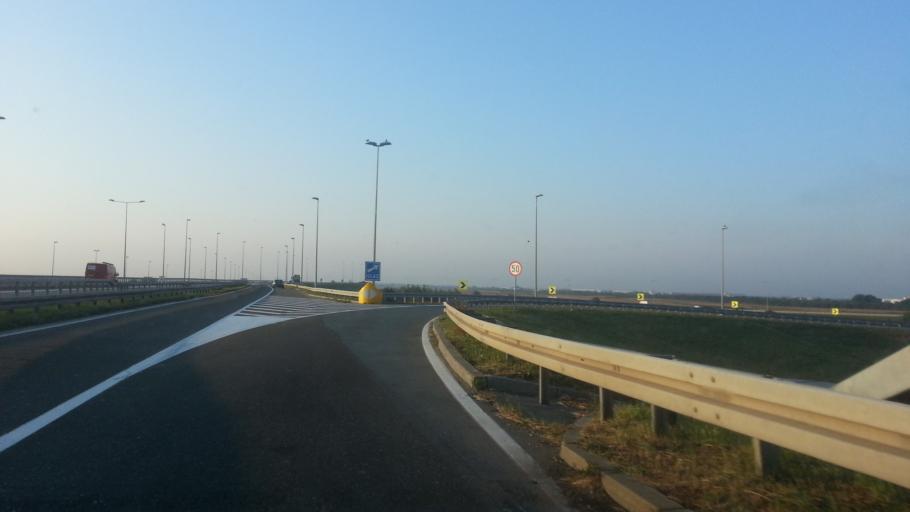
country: RS
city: Dobanovci
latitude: 44.8353
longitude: 20.2504
